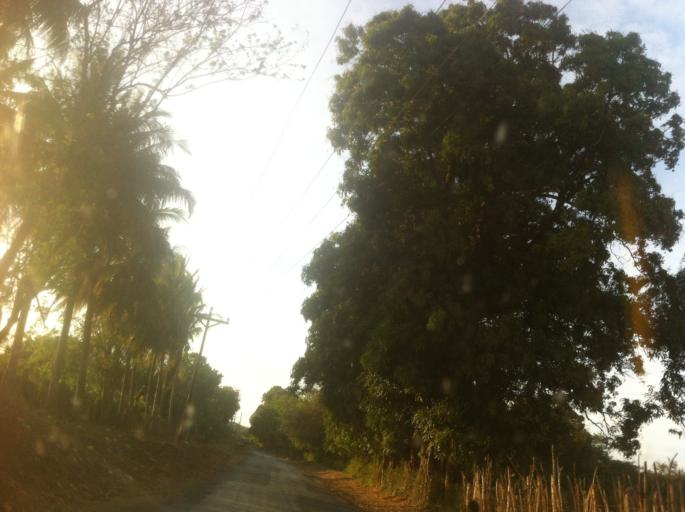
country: NI
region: Rivas
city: Potosi
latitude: 11.4949
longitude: -85.8605
